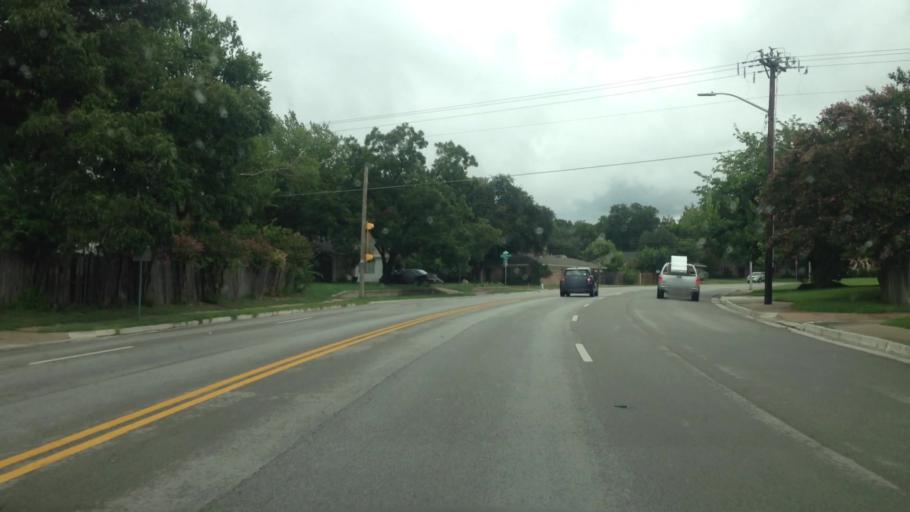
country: US
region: Texas
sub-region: Tarrant County
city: Edgecliff Village
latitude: 32.6585
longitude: -97.3976
